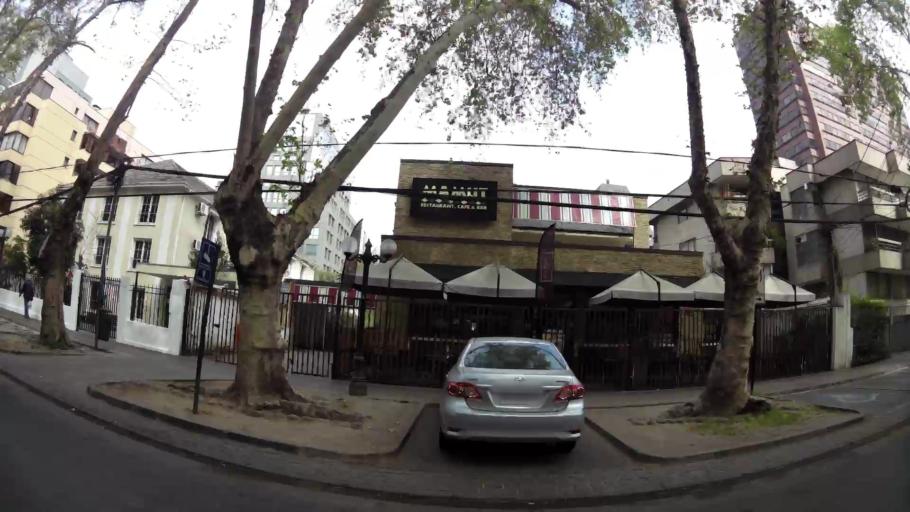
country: CL
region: Santiago Metropolitan
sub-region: Provincia de Santiago
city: Villa Presidente Frei, Nunoa, Santiago, Chile
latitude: -33.4196
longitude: -70.6012
